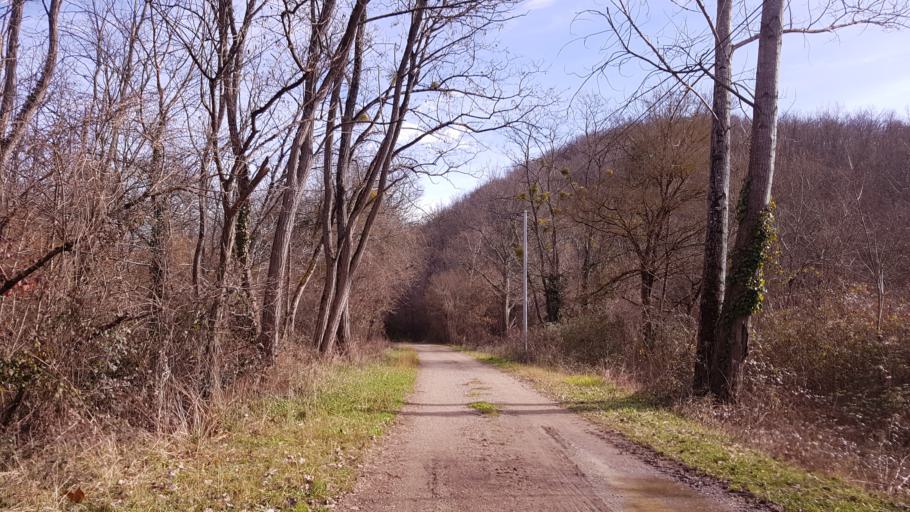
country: FR
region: Languedoc-Roussillon
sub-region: Departement de l'Aude
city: Chalabre
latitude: 43.0086
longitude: 1.9653
